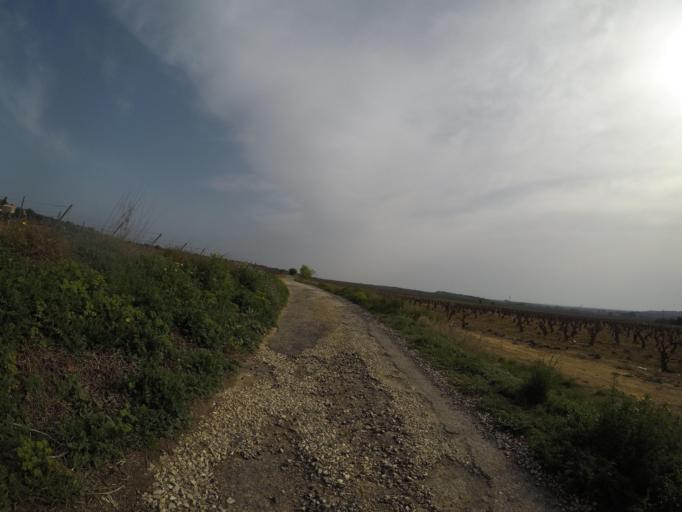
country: FR
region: Languedoc-Roussillon
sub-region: Departement des Pyrenees-Orientales
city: Baixas
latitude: 42.7575
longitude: 2.8161
